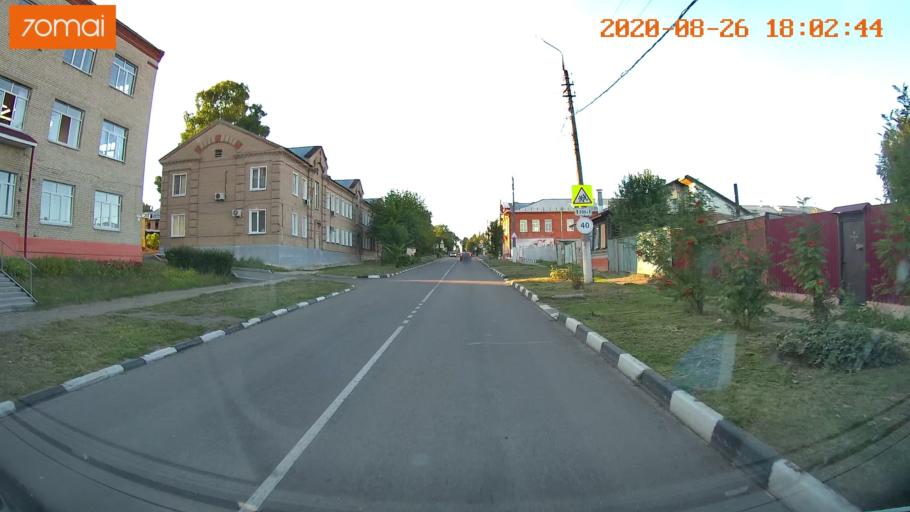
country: RU
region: Tula
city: Yefremov
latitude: 53.1404
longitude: 38.1210
